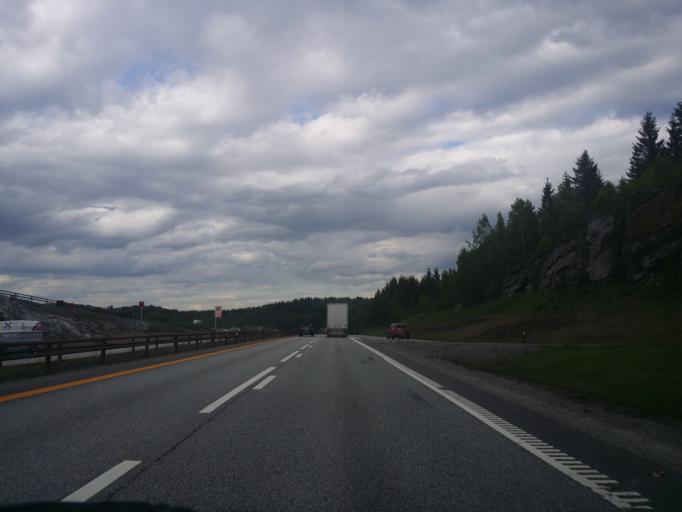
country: NO
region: Akershus
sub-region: Eidsvoll
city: Raholt
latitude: 60.3146
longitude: 11.1470
